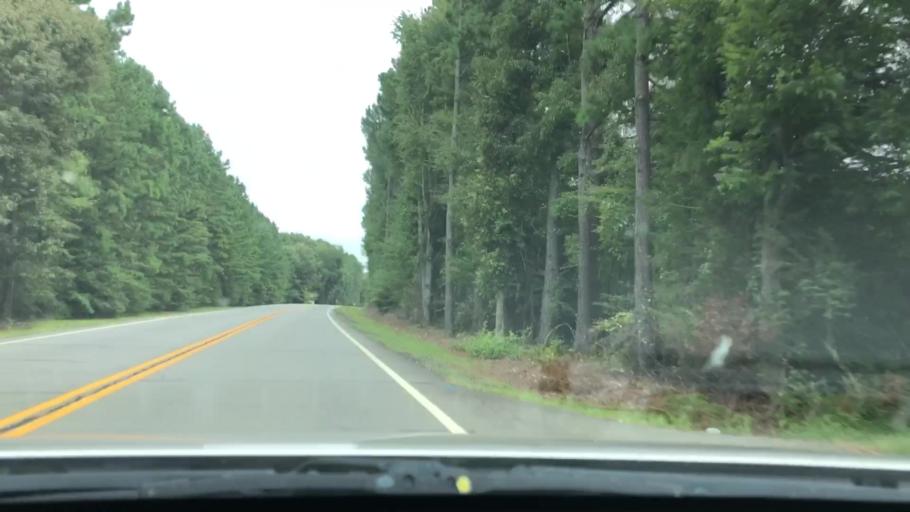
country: US
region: Georgia
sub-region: Upson County
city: Hannahs Mill
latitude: 33.0200
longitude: -84.4975
